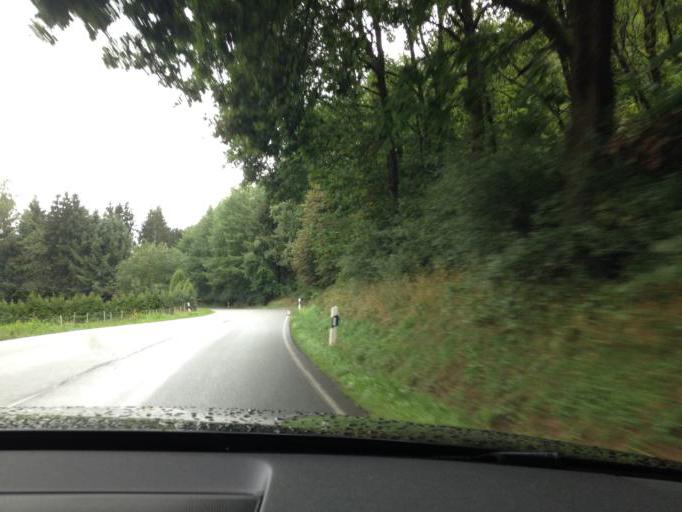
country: DE
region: Saarland
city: Sankt Wendel
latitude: 49.4788
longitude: 7.1532
